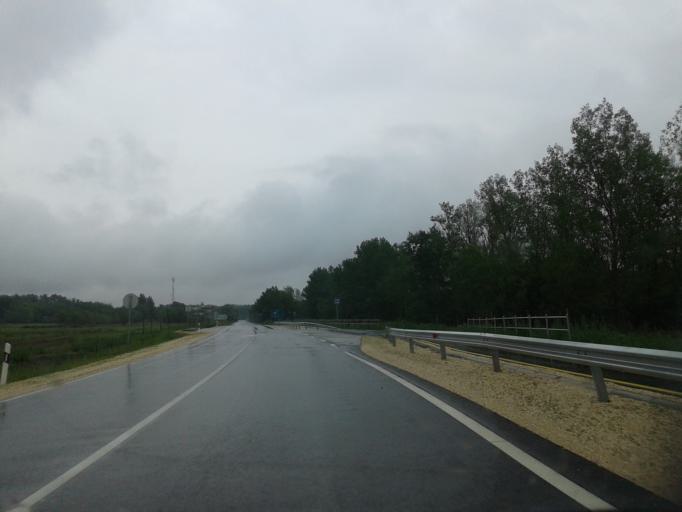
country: HU
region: Bacs-Kiskun
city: Kelebia
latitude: 46.2524
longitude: 19.6508
